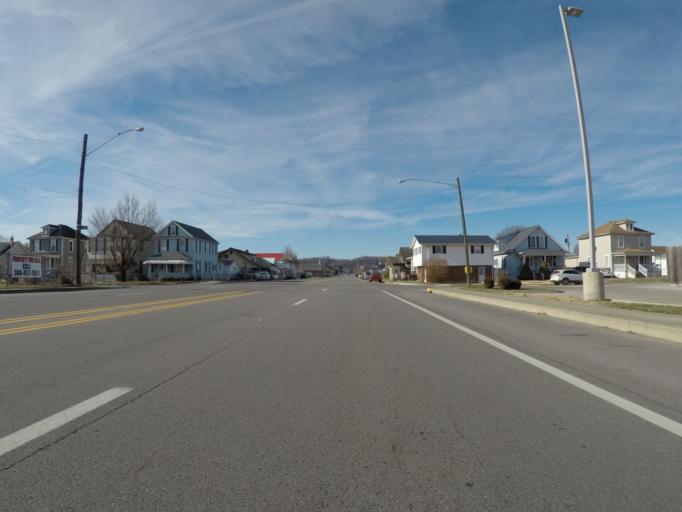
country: US
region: West Virginia
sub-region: Wayne County
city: Kenova
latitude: 38.4013
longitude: -82.5778
